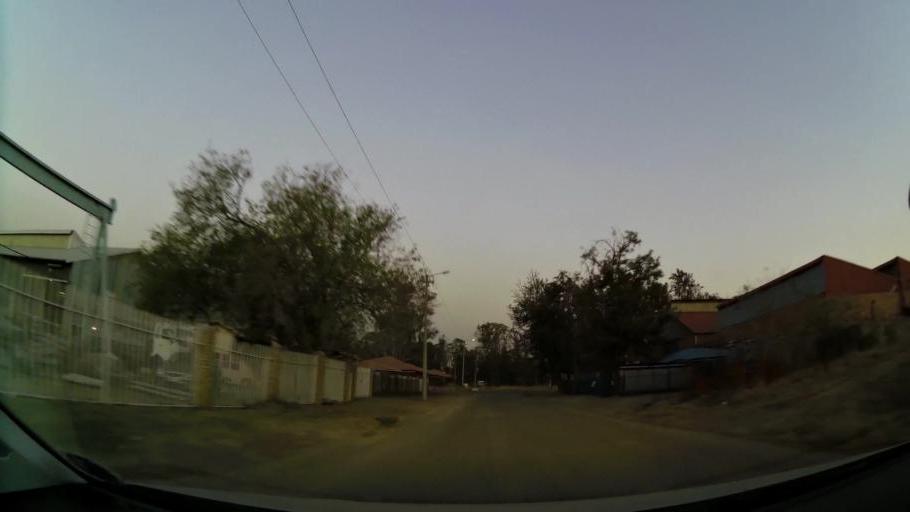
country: ZA
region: North-West
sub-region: Bojanala Platinum District Municipality
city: Rustenburg
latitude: -25.6721
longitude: 27.2613
